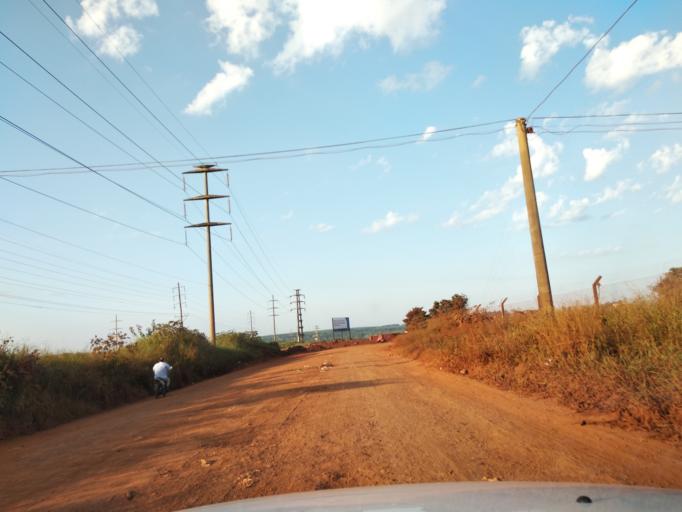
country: AR
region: Misiones
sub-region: Departamento de Capital
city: Posadas
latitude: -27.4443
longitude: -55.9166
